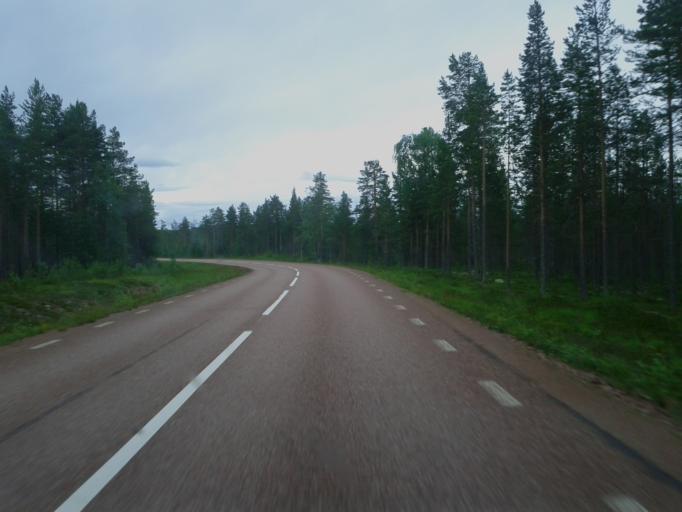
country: SE
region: Dalarna
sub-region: Alvdalens Kommun
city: AElvdalen
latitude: 61.5373
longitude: 13.3453
